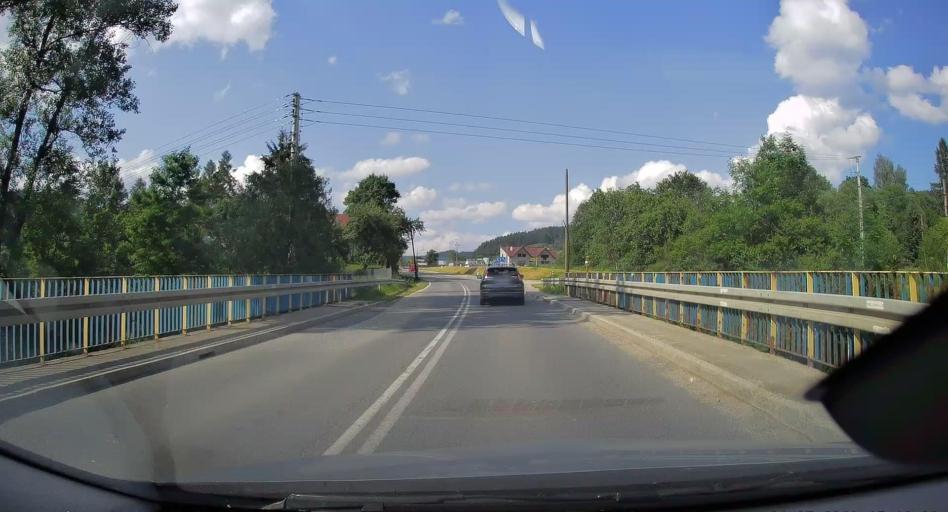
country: PL
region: Lesser Poland Voivodeship
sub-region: Powiat nowosadecki
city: Krynica-Zdroj
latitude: 49.3725
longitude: 20.9500
